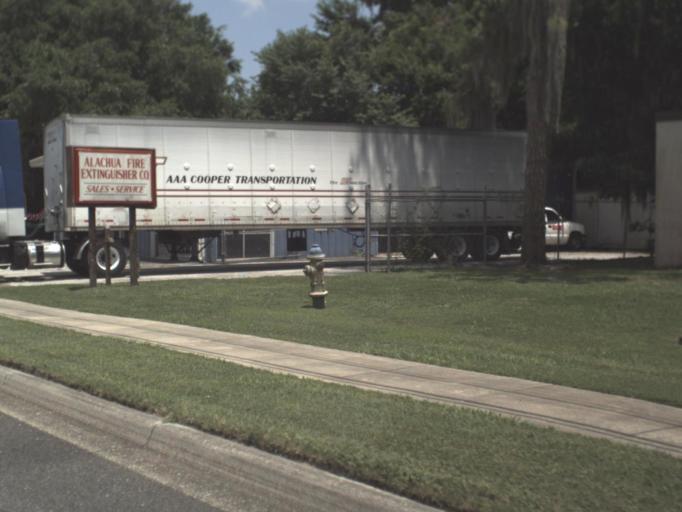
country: US
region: Florida
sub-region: Alachua County
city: Gainesville
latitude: 29.6074
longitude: -82.3658
